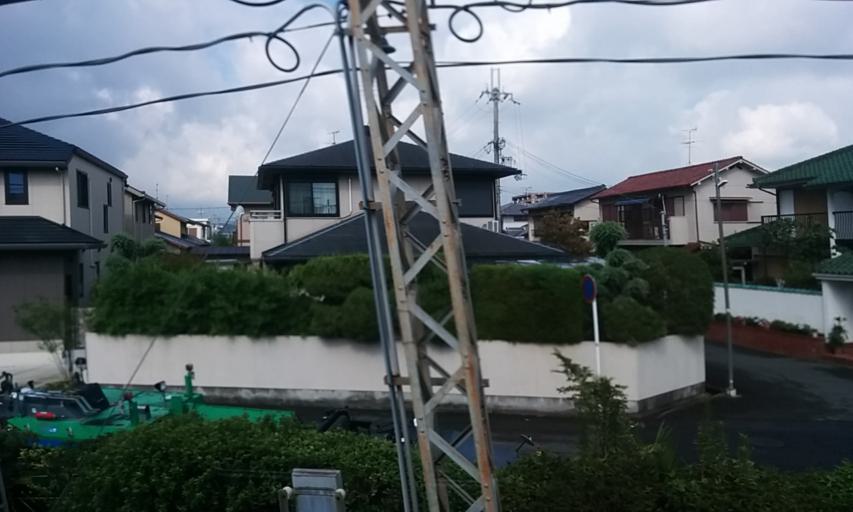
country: JP
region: Nara
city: Nara-shi
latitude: 34.6881
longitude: 135.7855
